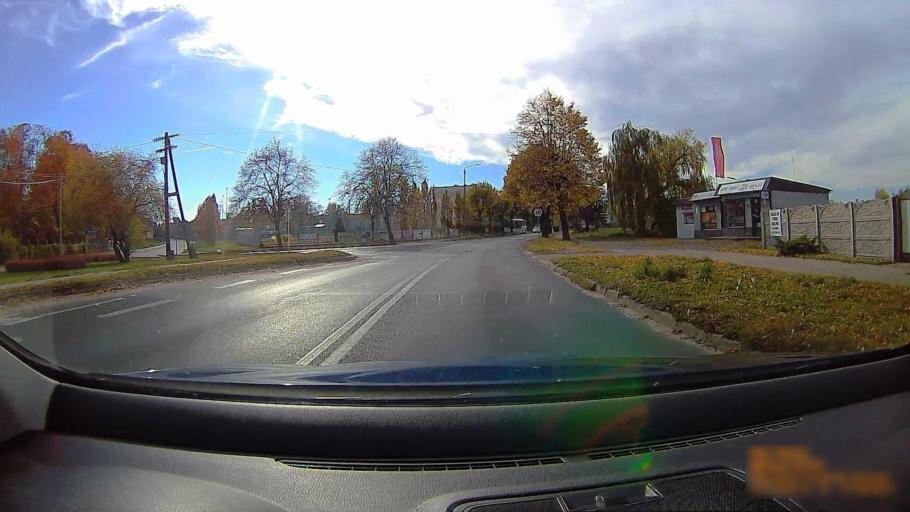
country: PL
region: Greater Poland Voivodeship
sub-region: Powiat ostrzeszowski
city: Ostrzeszow
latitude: 51.4252
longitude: 17.9385
